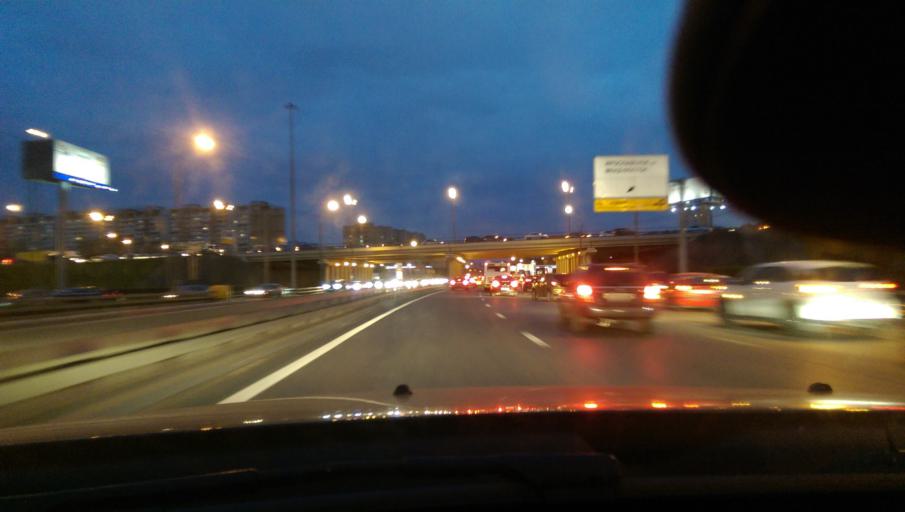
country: RU
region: Moscow
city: Vatutino
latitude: 55.8964
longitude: 37.6728
